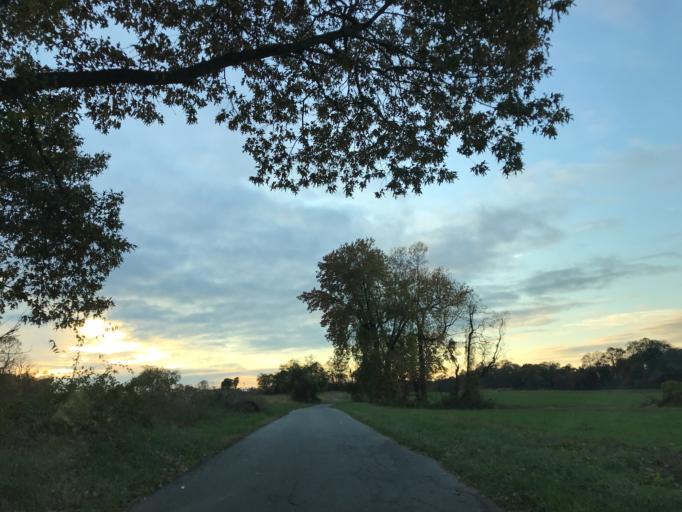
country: US
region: Maryland
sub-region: Baltimore County
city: White Marsh
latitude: 39.3771
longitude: -76.3983
